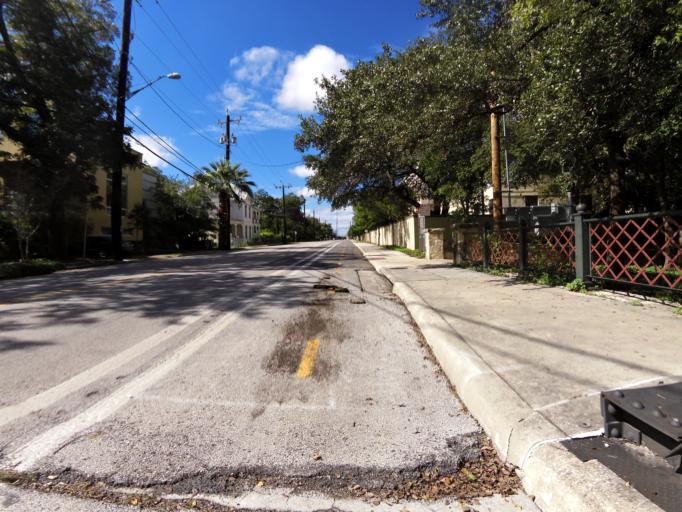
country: US
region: Texas
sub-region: Bexar County
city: San Antonio
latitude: 29.4156
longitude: -98.4941
